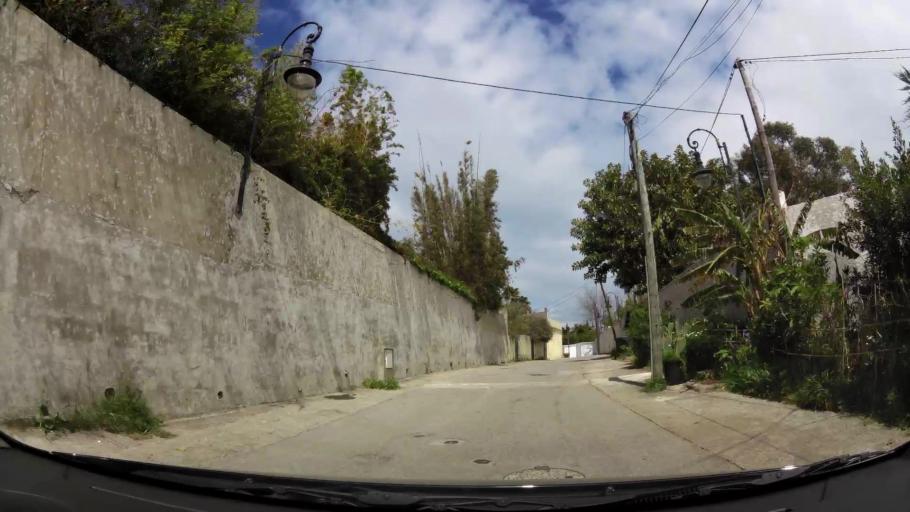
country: MA
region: Tanger-Tetouan
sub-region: Tanger-Assilah
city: Tangier
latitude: 35.7887
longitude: -5.8515
